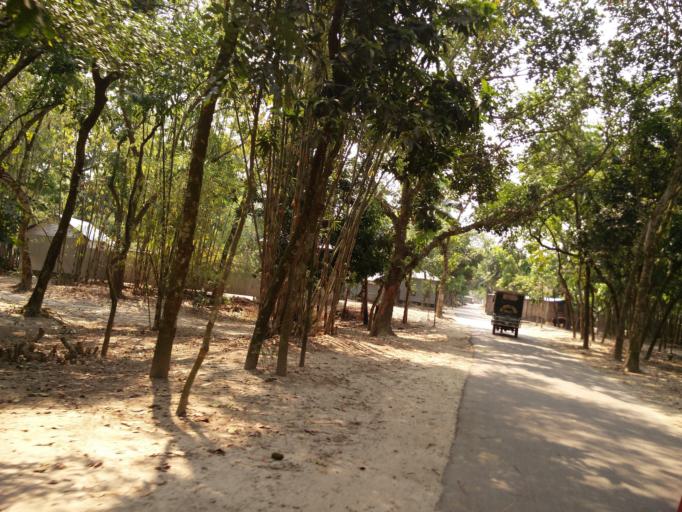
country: BD
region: Dhaka
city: Muktagacha
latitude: 24.9097
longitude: 90.2552
